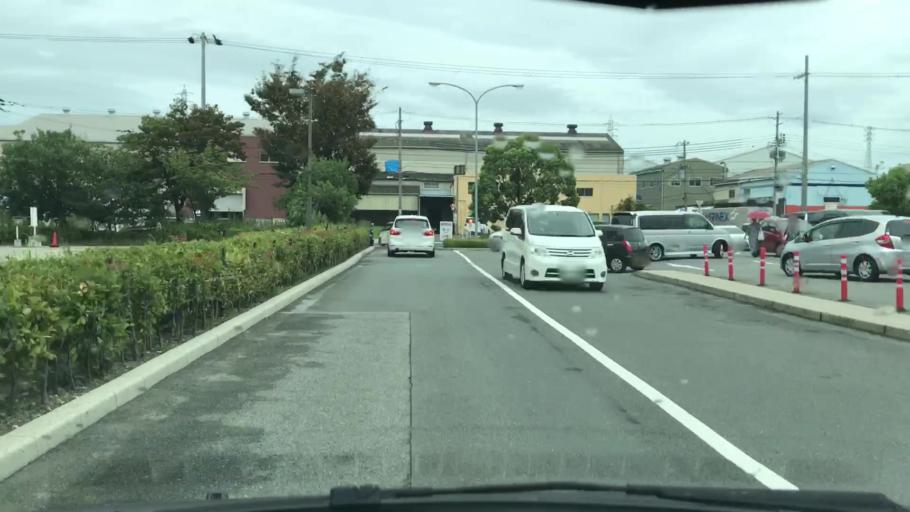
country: JP
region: Hyogo
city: Amagasaki
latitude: 34.7423
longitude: 135.4433
